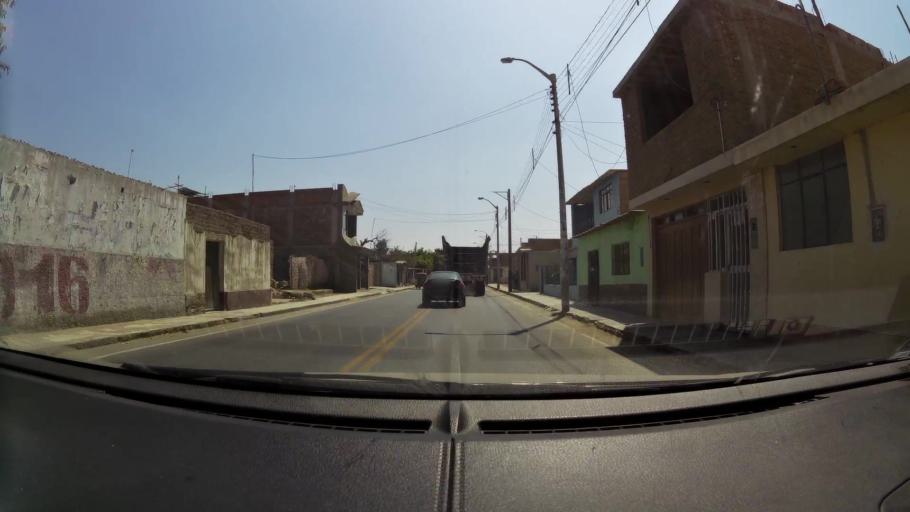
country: PE
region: Lambayeque
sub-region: Provincia de Chiclayo
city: Mocupe
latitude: -6.9903
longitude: -79.6237
